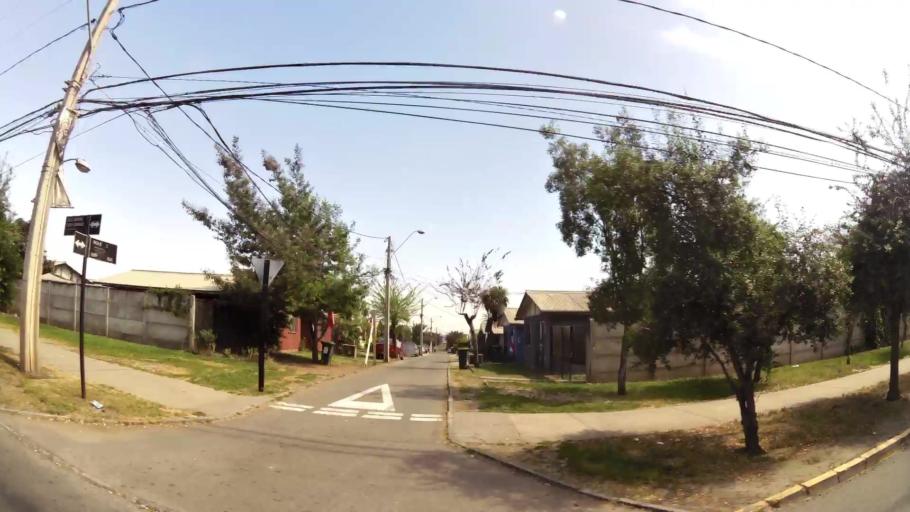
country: CL
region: Santiago Metropolitan
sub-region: Provincia de Santiago
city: Villa Presidente Frei, Nunoa, Santiago, Chile
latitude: -33.4618
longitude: -70.5415
